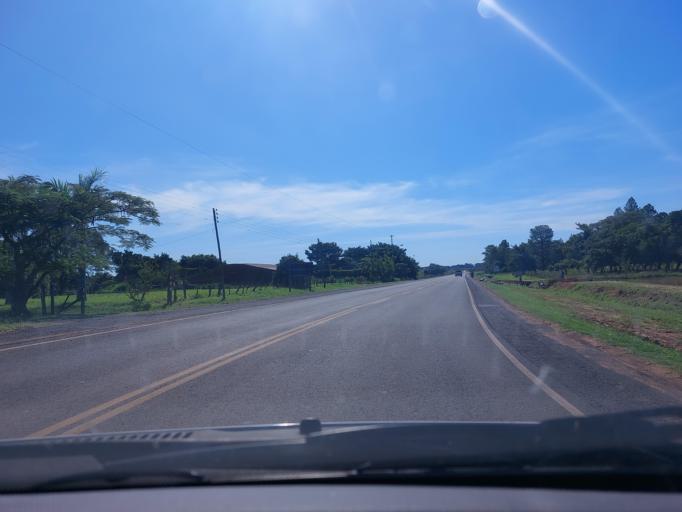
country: PY
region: San Pedro
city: Itacurubi del Rosario
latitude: -24.6063
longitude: -56.7906
